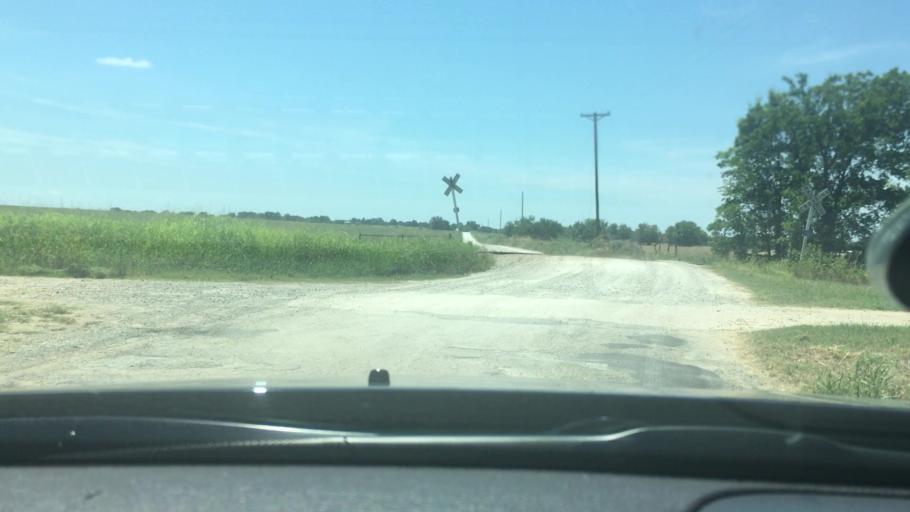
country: US
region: Oklahoma
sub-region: Bryan County
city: Durant
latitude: 34.0093
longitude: -96.1122
